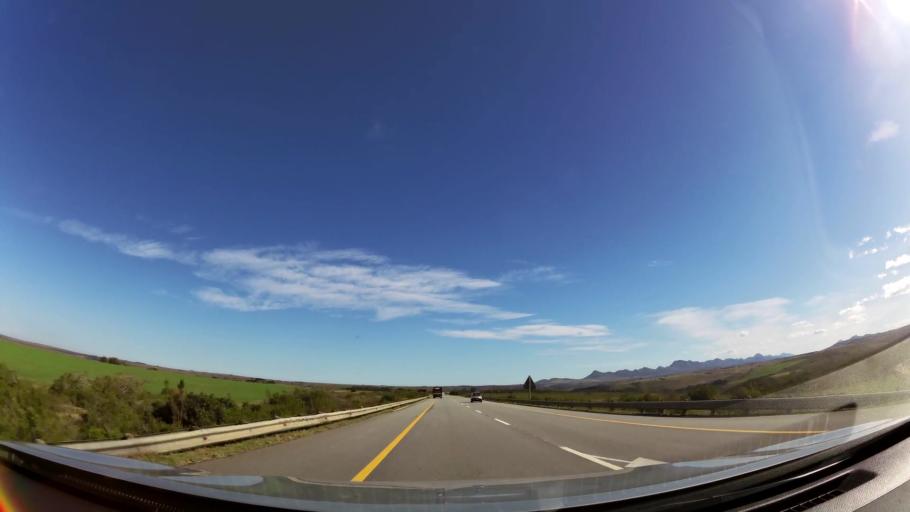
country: ZA
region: Eastern Cape
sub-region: Cacadu District Municipality
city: Kruisfontein
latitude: -34.0227
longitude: 24.6130
